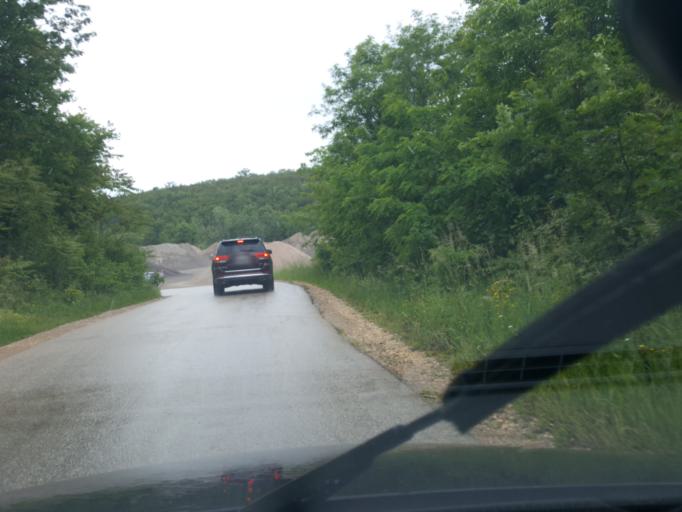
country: RS
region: Central Serbia
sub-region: Zajecarski Okrug
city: Boljevac
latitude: 43.7990
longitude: 21.9012
